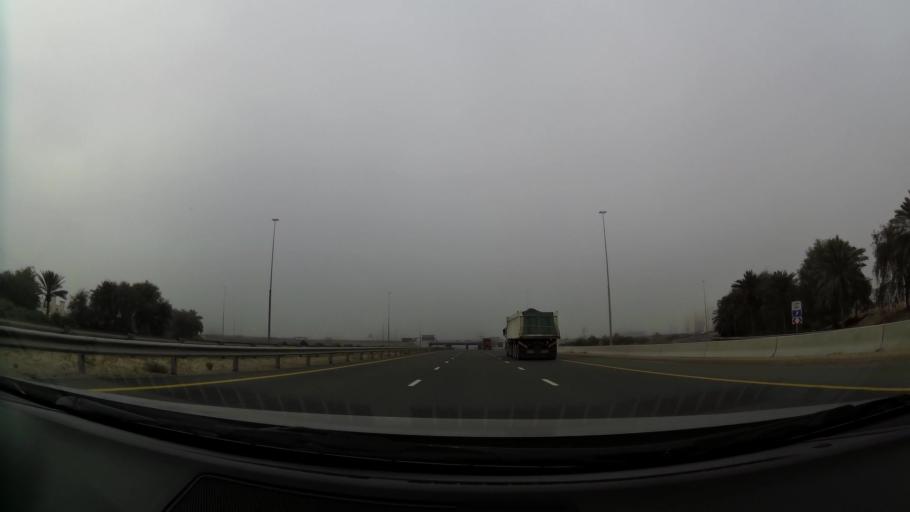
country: AE
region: Dubai
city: Dubai
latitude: 25.1229
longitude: 55.3622
